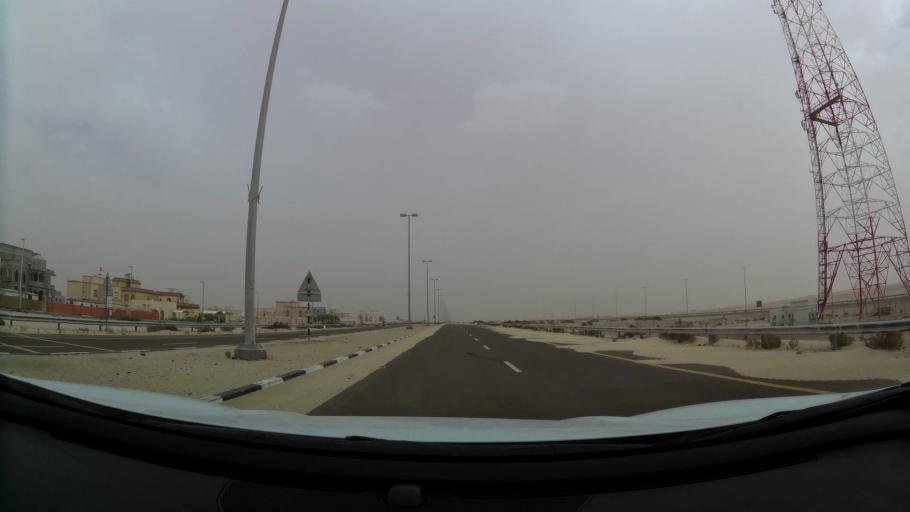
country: AE
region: Abu Dhabi
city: Abu Dhabi
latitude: 24.3545
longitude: 54.7117
